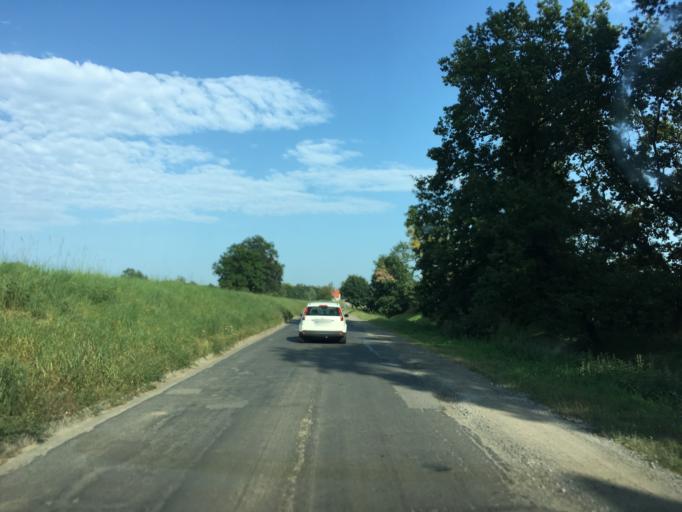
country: PL
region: Lower Silesian Voivodeship
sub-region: Powiat wroclawski
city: Radwanice
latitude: 51.0952
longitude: 17.1185
